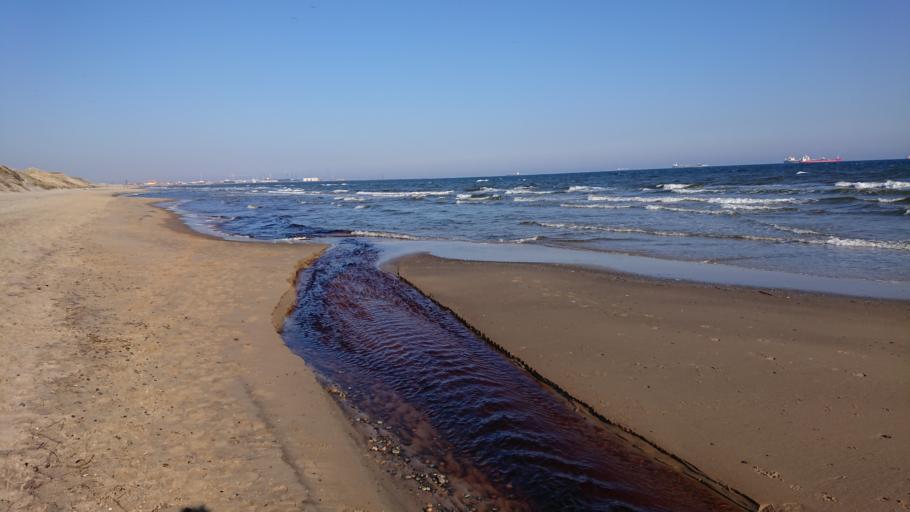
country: DK
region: North Denmark
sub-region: Frederikshavn Kommune
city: Skagen
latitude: 57.7009
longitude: 10.5466
